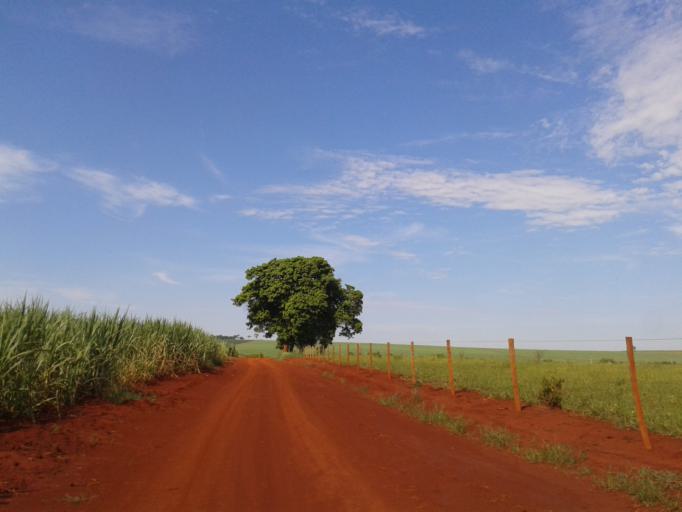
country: BR
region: Minas Gerais
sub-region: Centralina
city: Centralina
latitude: -18.6351
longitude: -49.2513
